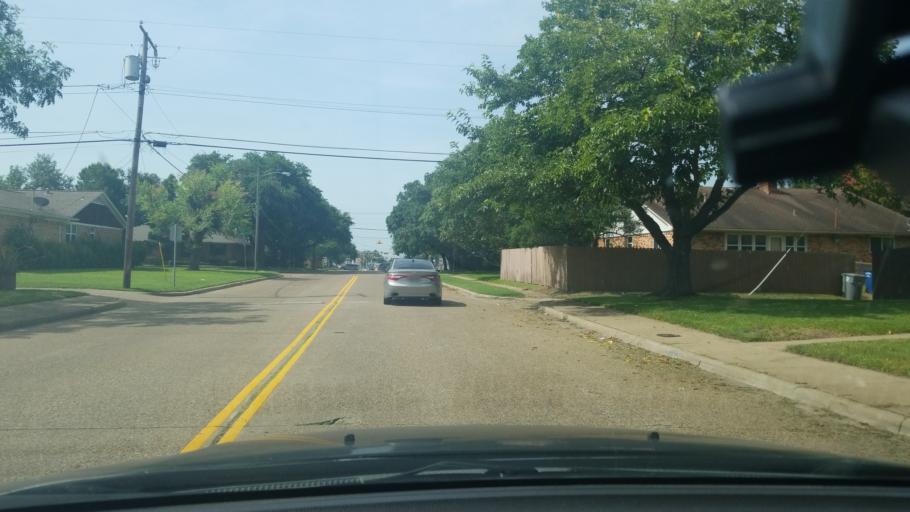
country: US
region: Texas
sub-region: Dallas County
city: Highland Park
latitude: 32.7969
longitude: -96.6999
